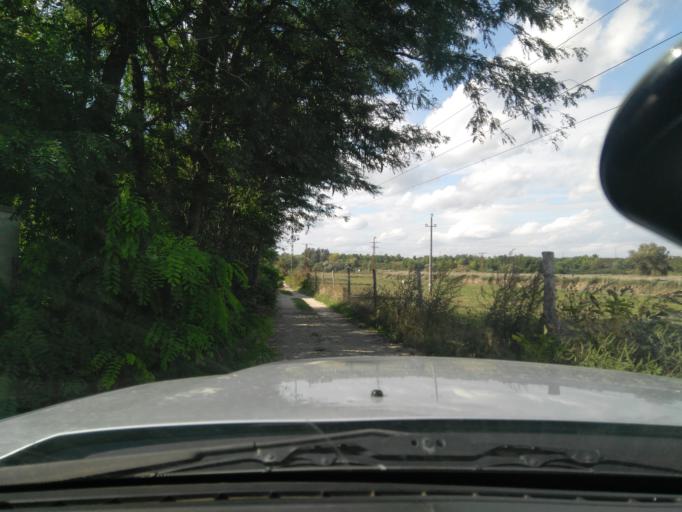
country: HU
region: Fejer
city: Bicske
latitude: 47.4852
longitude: 18.6553
